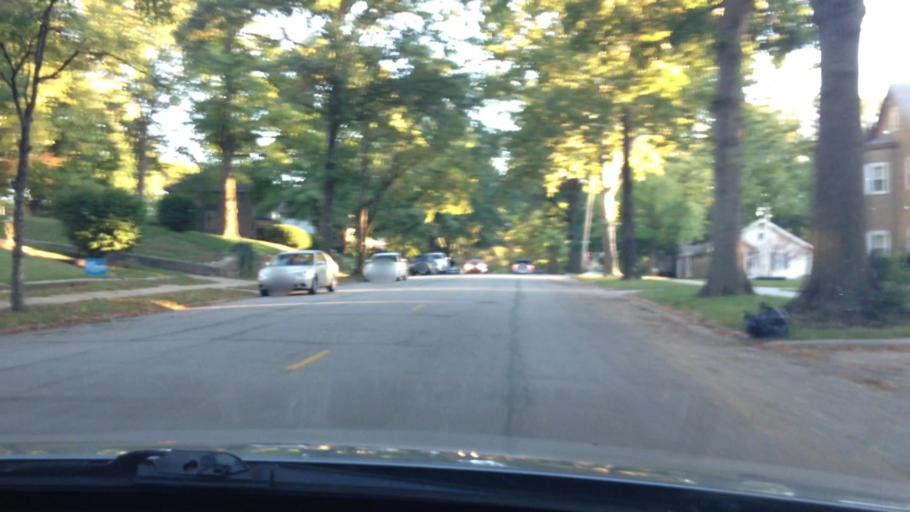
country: US
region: Kansas
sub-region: Leavenworth County
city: Leavenworth
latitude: 39.3058
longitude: -94.9208
